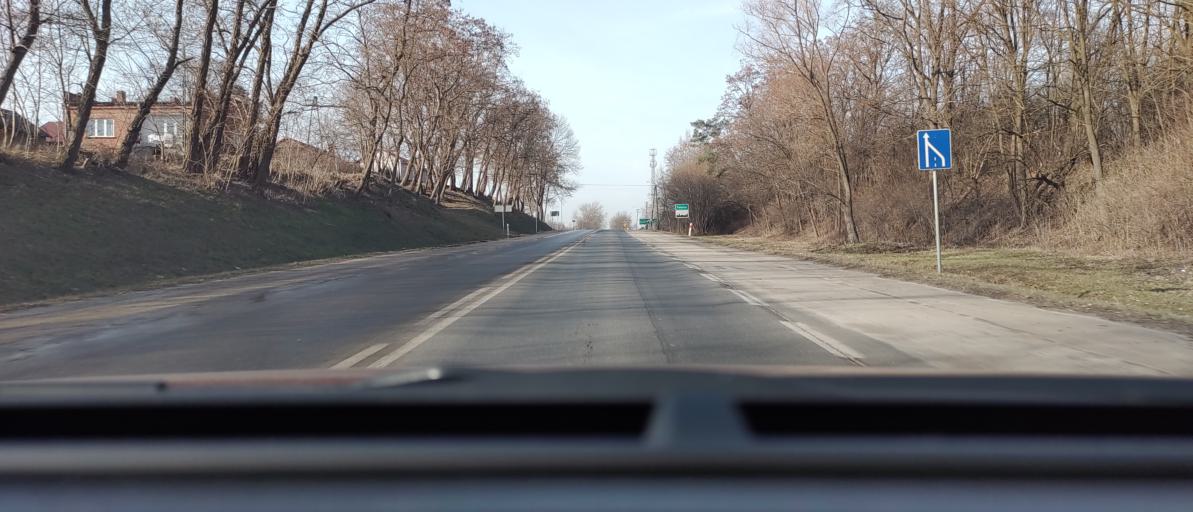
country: PL
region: Masovian Voivodeship
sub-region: Powiat bialobrzeski
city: Promna
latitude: 51.6720
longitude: 20.9440
